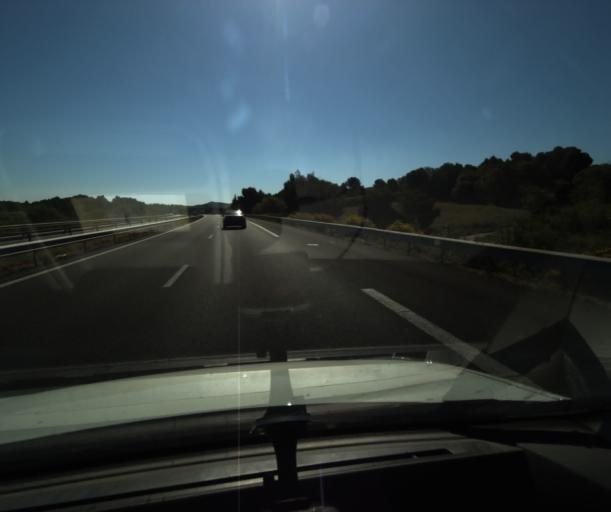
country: FR
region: Languedoc-Roussillon
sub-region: Departement de l'Aude
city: Capendu
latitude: 43.1784
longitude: 2.5709
